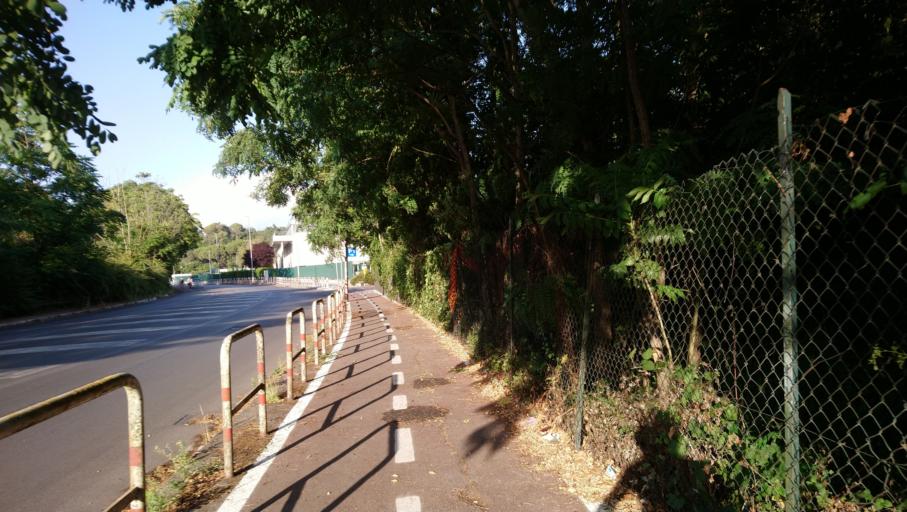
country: IT
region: Latium
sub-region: Citta metropolitana di Roma Capitale
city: Rome
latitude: 41.9318
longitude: 12.4897
